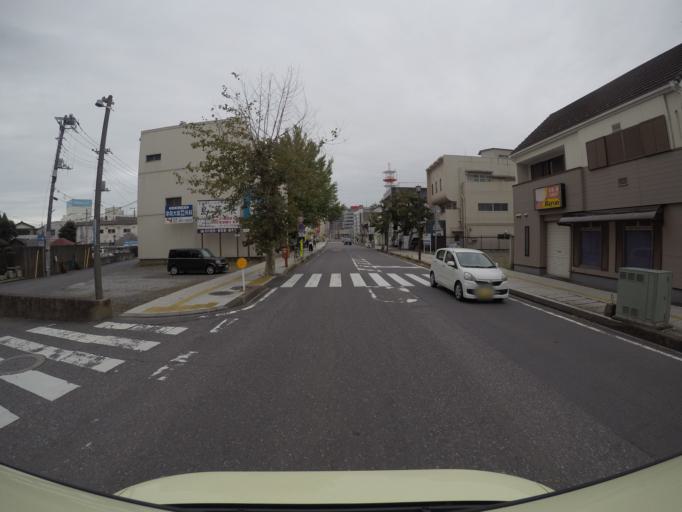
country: JP
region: Ibaraki
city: Naka
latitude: 36.0838
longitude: 140.2004
